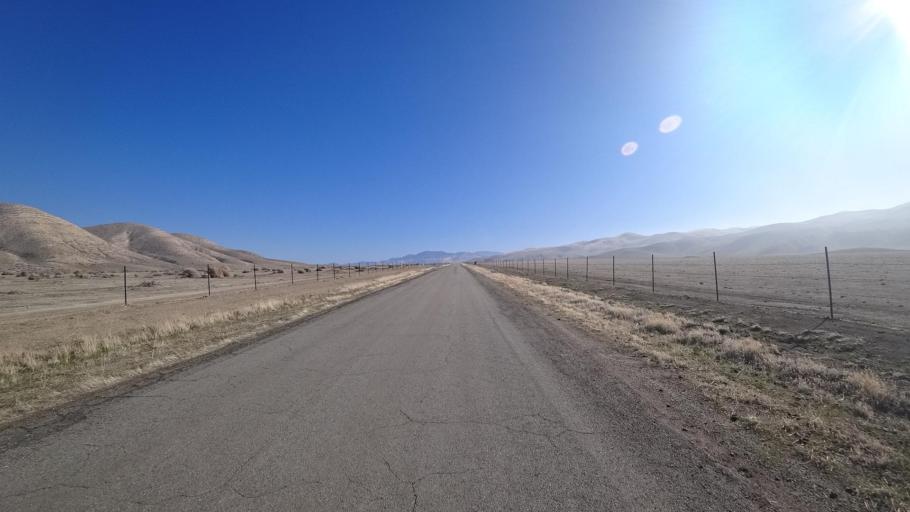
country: US
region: California
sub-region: Kern County
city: Maricopa
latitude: 35.0009
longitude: -119.4031
